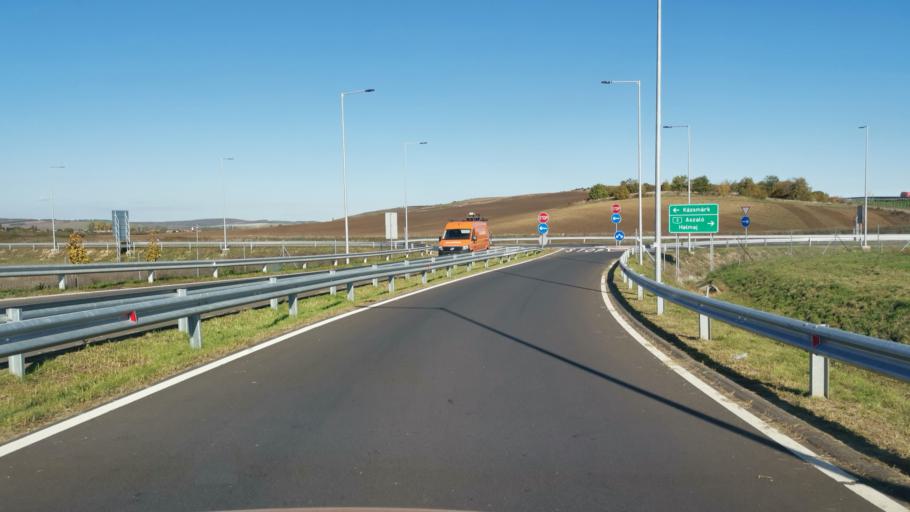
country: HU
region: Borsod-Abauj-Zemplen
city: Halmaj
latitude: 48.2543
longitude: 20.9776
